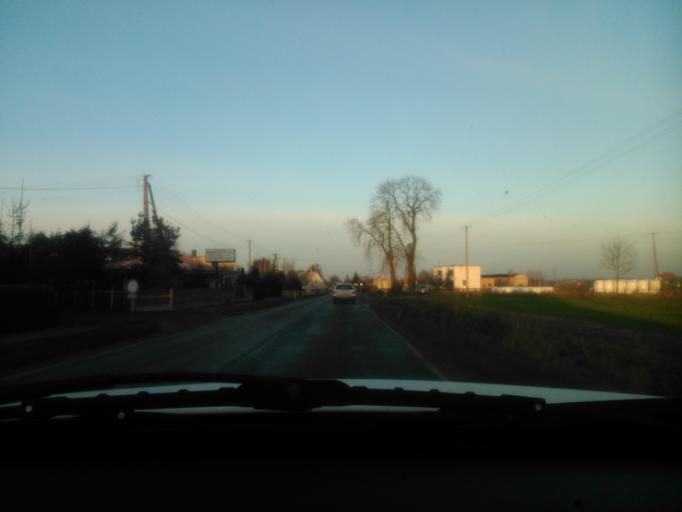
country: PL
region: Kujawsko-Pomorskie
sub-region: Powiat golubsko-dobrzynski
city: Kowalewo Pomorskie
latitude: 53.1444
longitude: 18.9785
